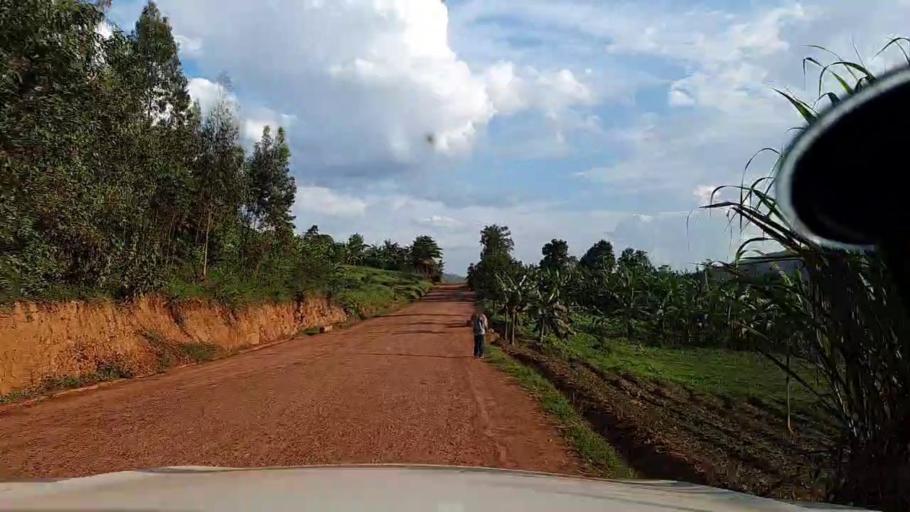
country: RW
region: Kigali
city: Kigali
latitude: -1.9250
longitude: 29.9905
